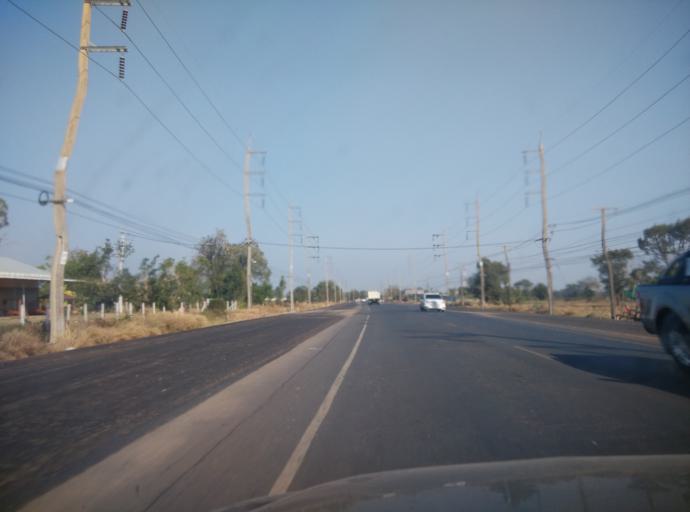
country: TH
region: Sisaket
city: Uthumphon Phisai
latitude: 15.1481
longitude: 104.2242
